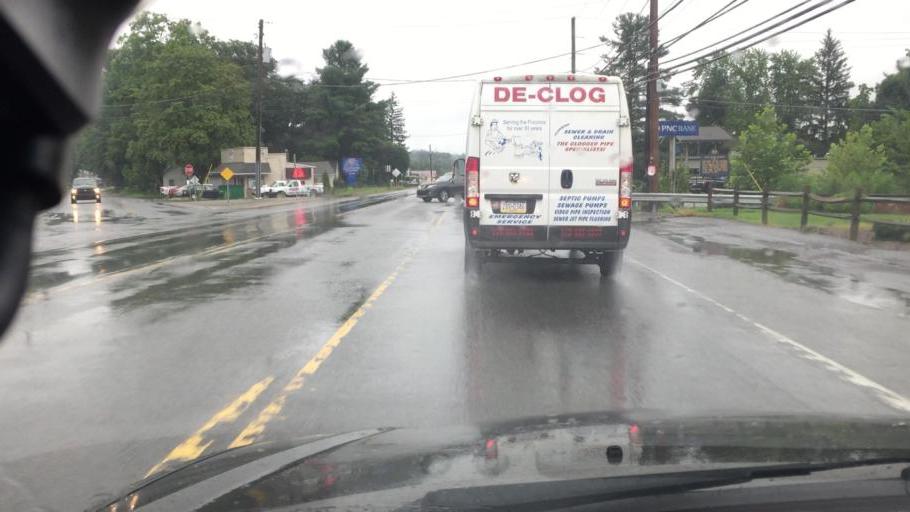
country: US
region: Pennsylvania
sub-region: Monroe County
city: Tannersville
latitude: 41.0401
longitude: -75.3061
